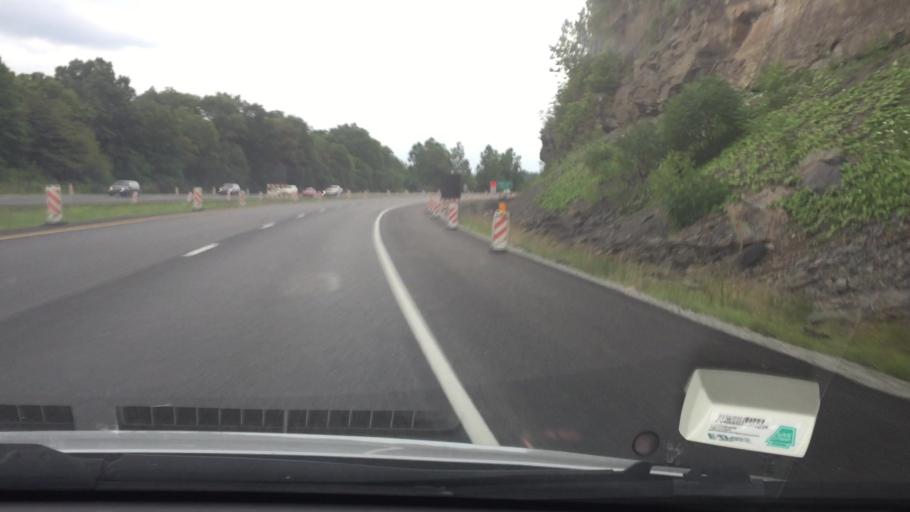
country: US
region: Pennsylvania
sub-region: Allegheny County
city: Brackenridge
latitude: 40.6433
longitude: -79.7201
